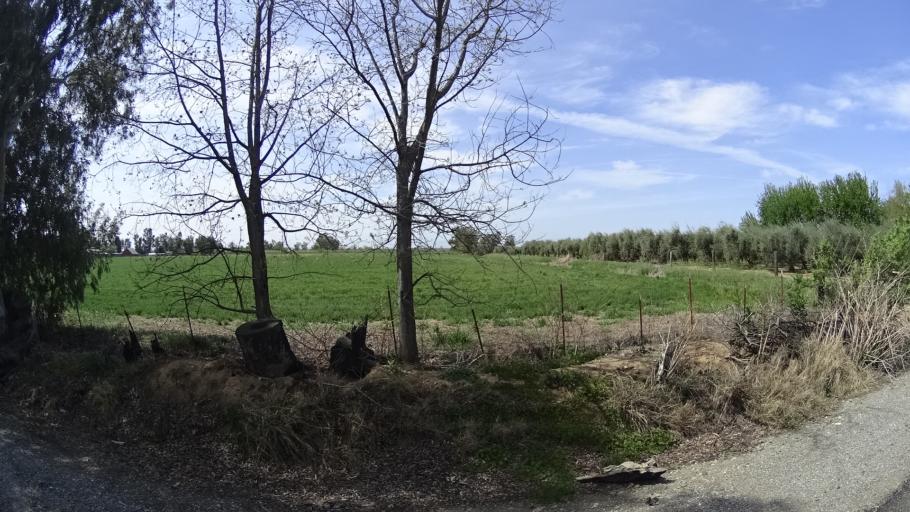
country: US
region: California
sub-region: Glenn County
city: Orland
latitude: 39.7903
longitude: -122.1504
